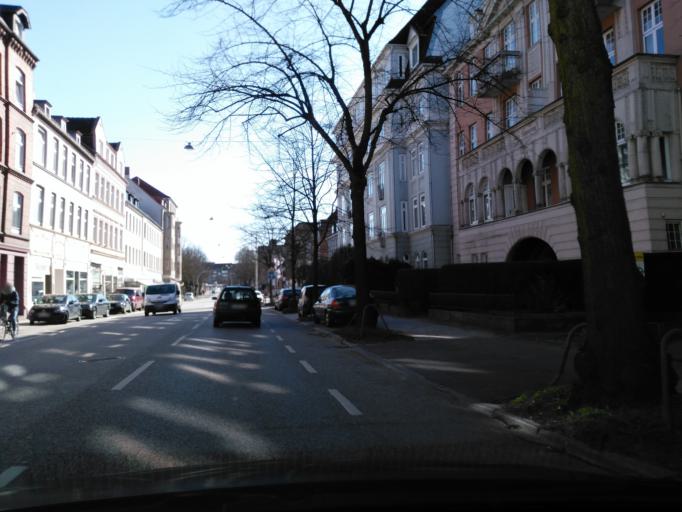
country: DE
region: Schleswig-Holstein
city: Kiel
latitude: 54.3251
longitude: 10.1275
